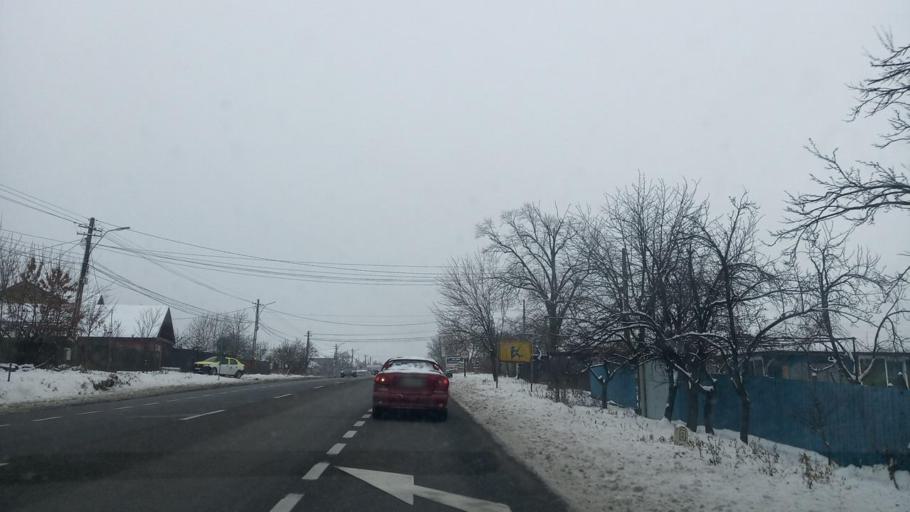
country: RO
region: Bacau
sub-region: Comuna Racaciuni
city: Gheorghe Doja
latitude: 46.3995
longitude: 26.9461
